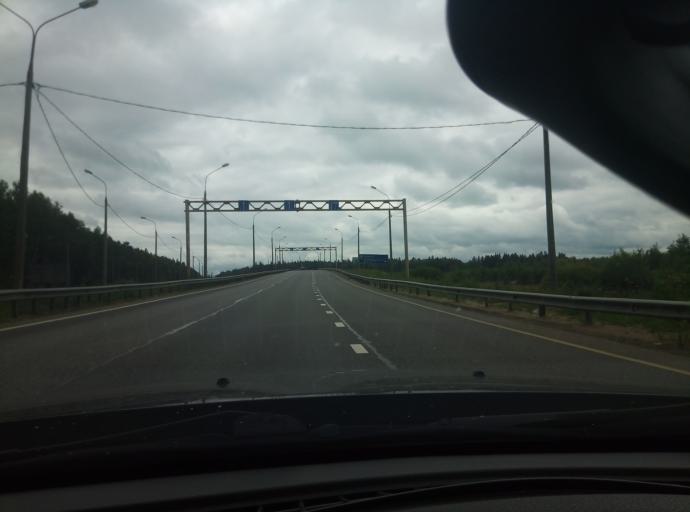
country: RU
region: Kaluga
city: Maloyaroslavets
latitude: 54.9818
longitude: 36.4971
